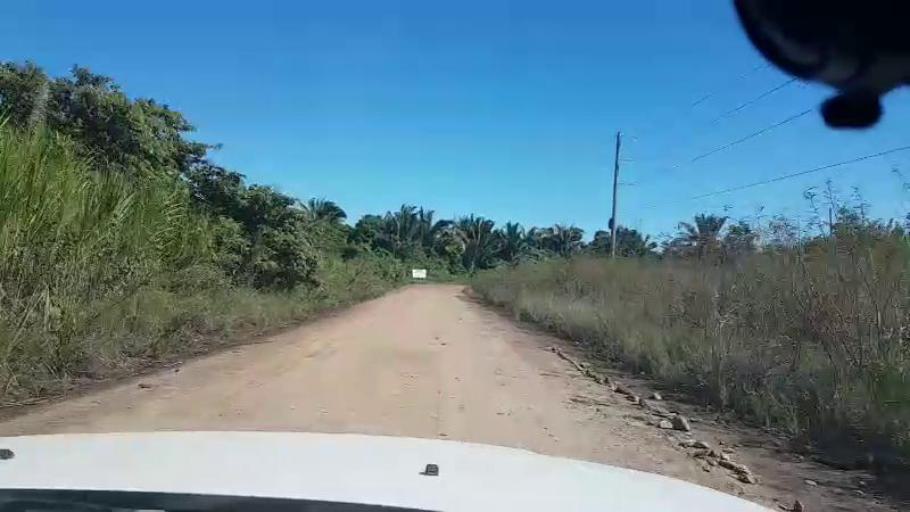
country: BZ
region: Stann Creek
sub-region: Dangriga
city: Dangriga
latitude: 17.1578
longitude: -88.3288
